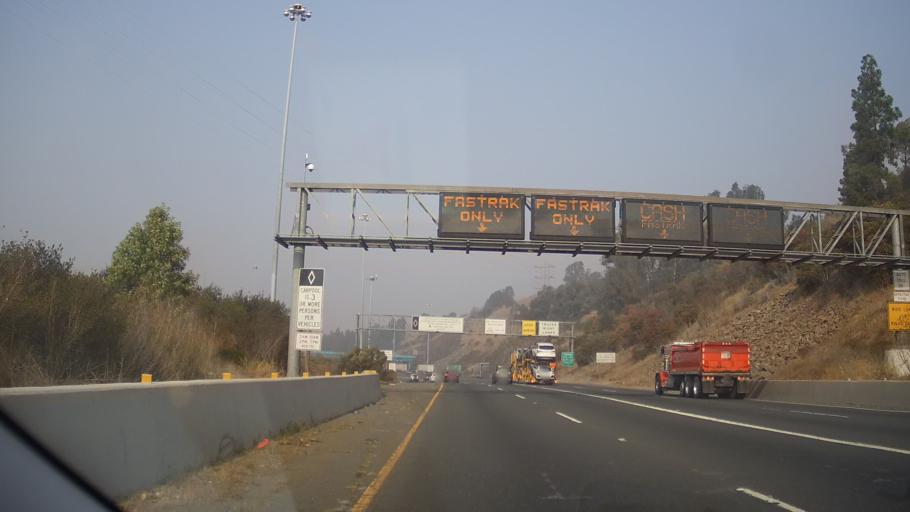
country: US
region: California
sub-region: Contra Costa County
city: Crockett
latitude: 38.0655
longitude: -122.2257
